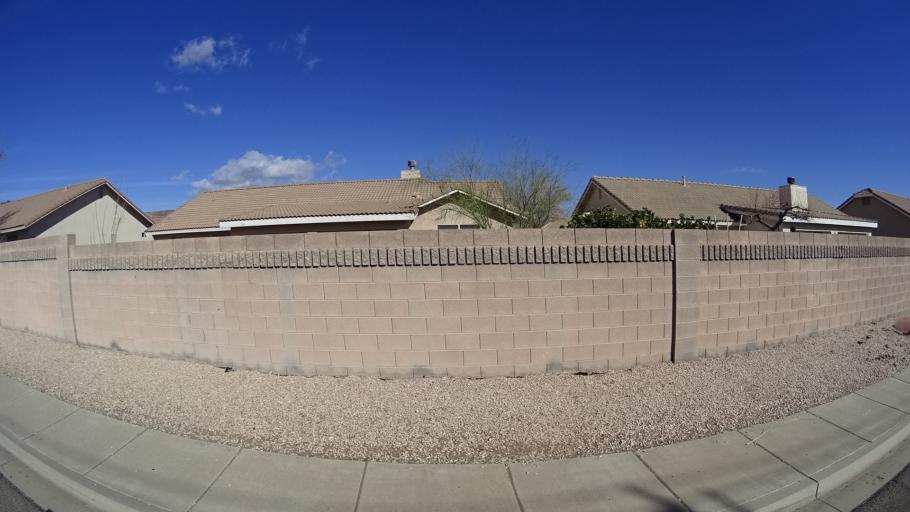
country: US
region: Arizona
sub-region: Mohave County
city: New Kingman-Butler
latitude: 35.2322
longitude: -114.0319
